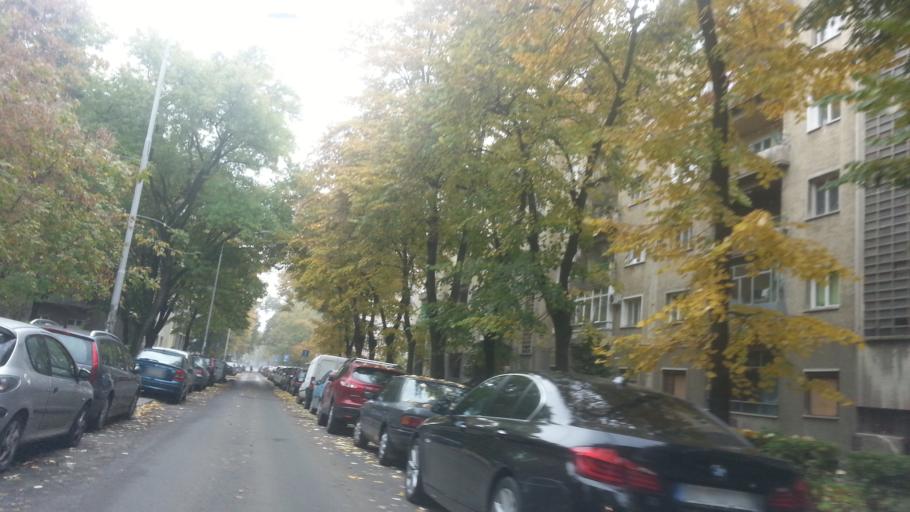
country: RS
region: Central Serbia
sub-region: Belgrade
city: Zemun
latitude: 44.8325
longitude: 20.4039
